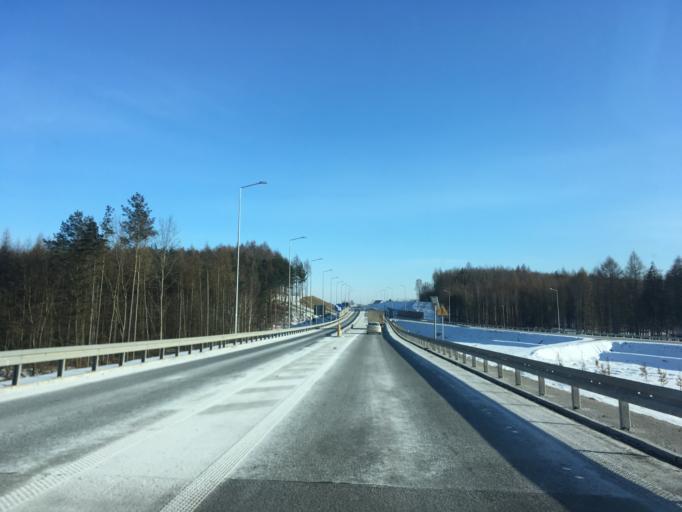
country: PL
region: Pomeranian Voivodeship
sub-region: Powiat koscierski
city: Koscierzyna
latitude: 54.1113
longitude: 17.9540
